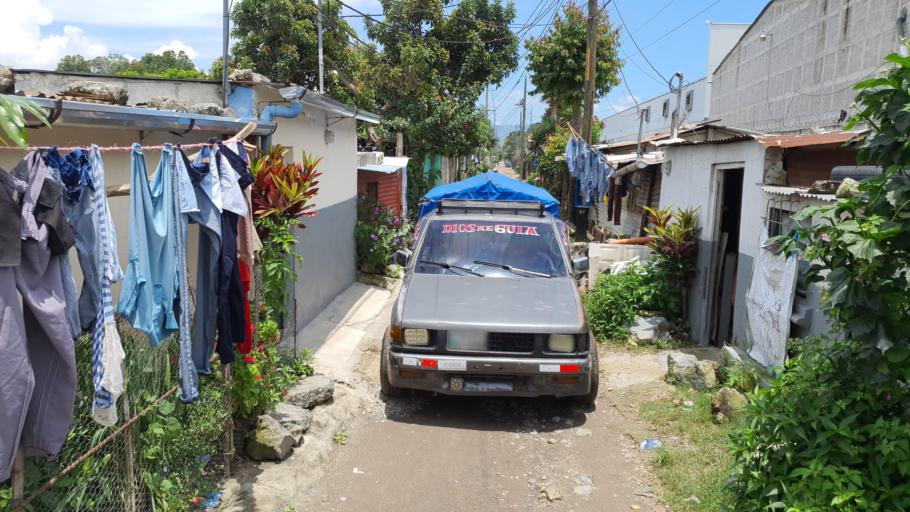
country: GT
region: Guatemala
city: Villa Canales
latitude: 14.4911
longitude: -90.5371
